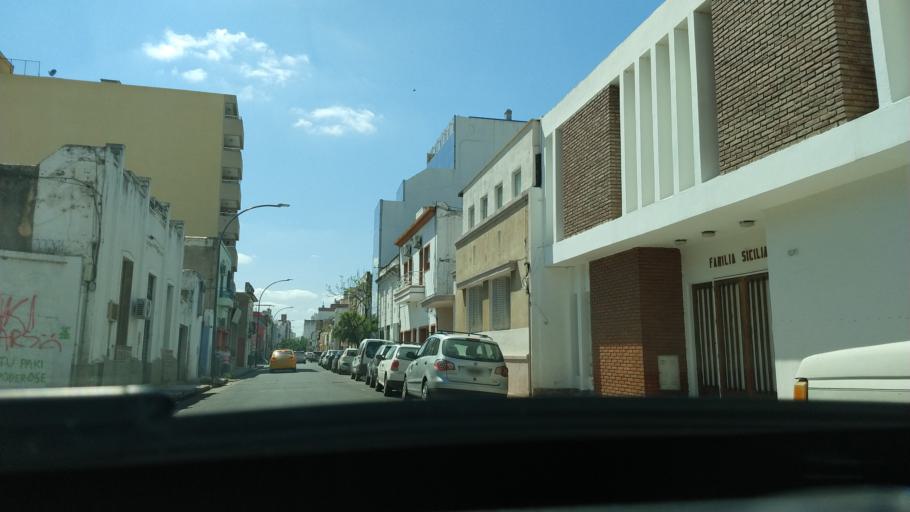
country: AR
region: Cordoba
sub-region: Departamento de Capital
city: Cordoba
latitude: -31.4071
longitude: -64.1968
